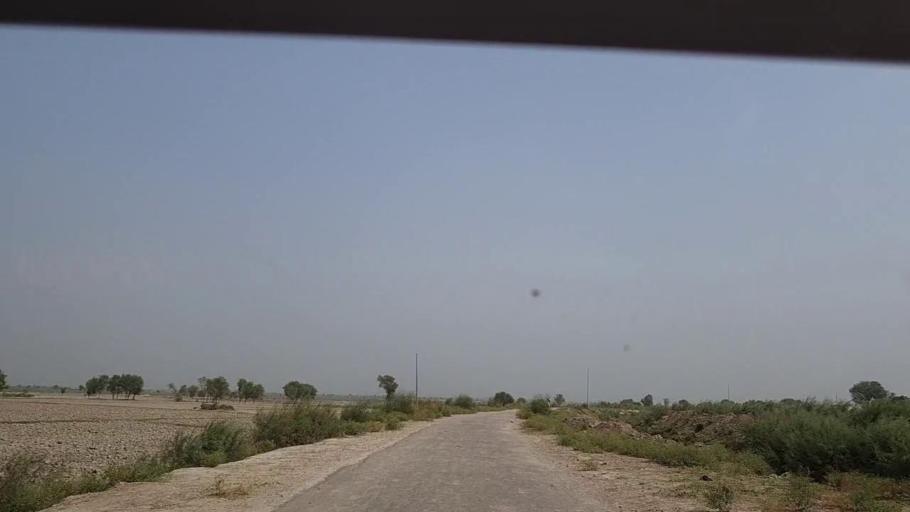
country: PK
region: Sindh
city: Khairpur Nathan Shah
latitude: 27.0455
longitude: 67.6856
